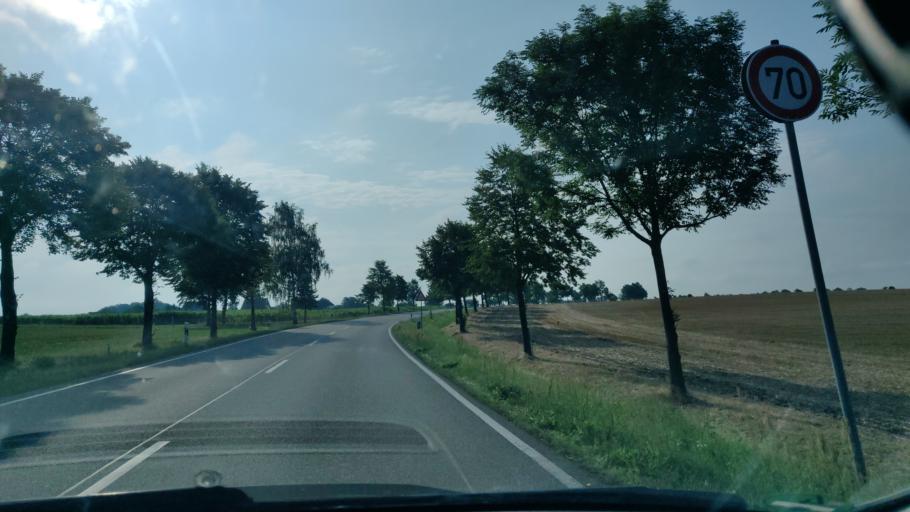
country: DE
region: Saxony
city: Bad Lausick
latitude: 51.1397
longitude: 12.6815
